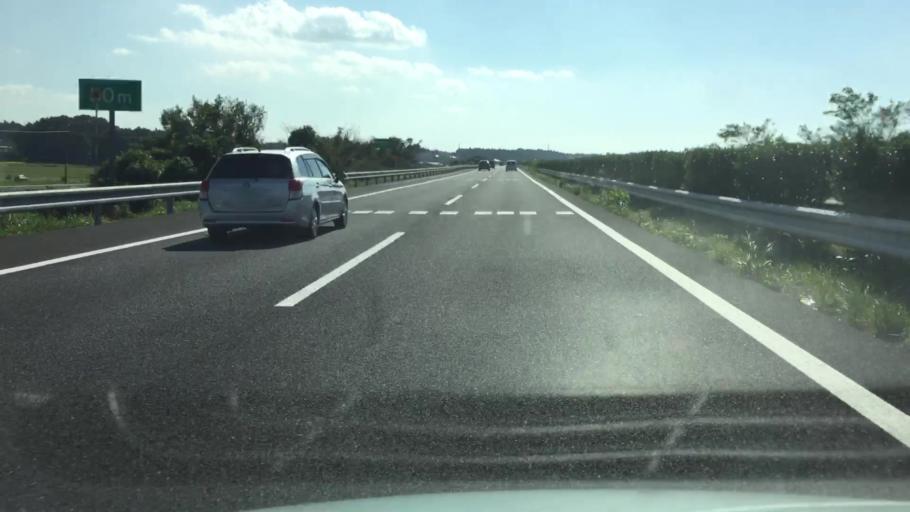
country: JP
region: Ibaraki
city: Tomobe
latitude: 36.3234
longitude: 140.3014
